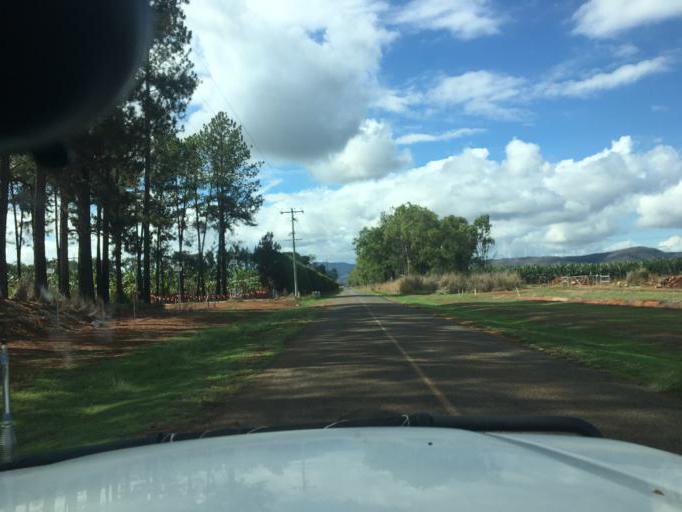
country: AU
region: Queensland
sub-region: Tablelands
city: Mareeba
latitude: -17.1068
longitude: 145.4111
